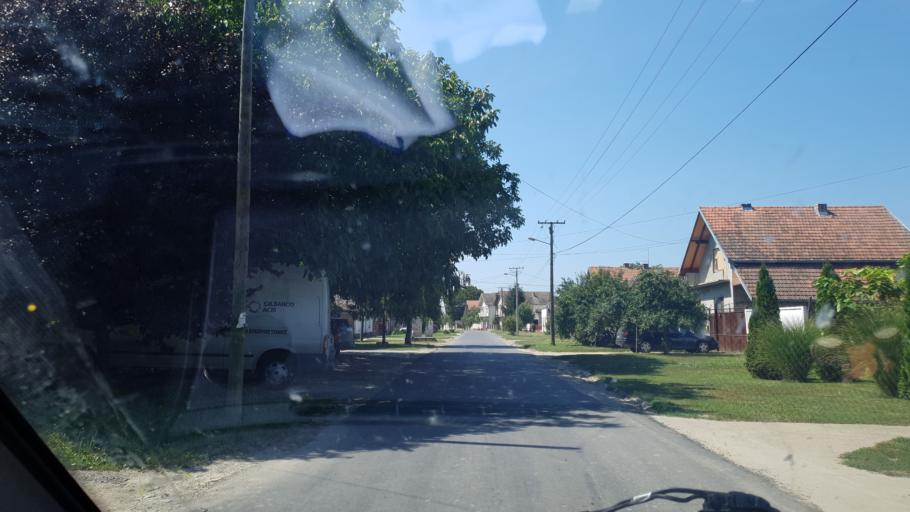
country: RS
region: Autonomna Pokrajina Vojvodina
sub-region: Juznobacki Okrug
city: Kovilj
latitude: 45.2252
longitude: 20.0255
